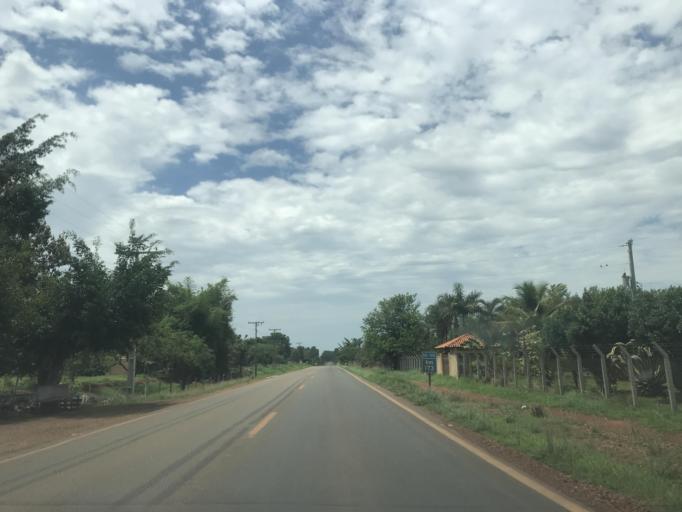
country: BR
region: Goias
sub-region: Luziania
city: Luziania
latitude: -16.3322
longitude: -48.0191
